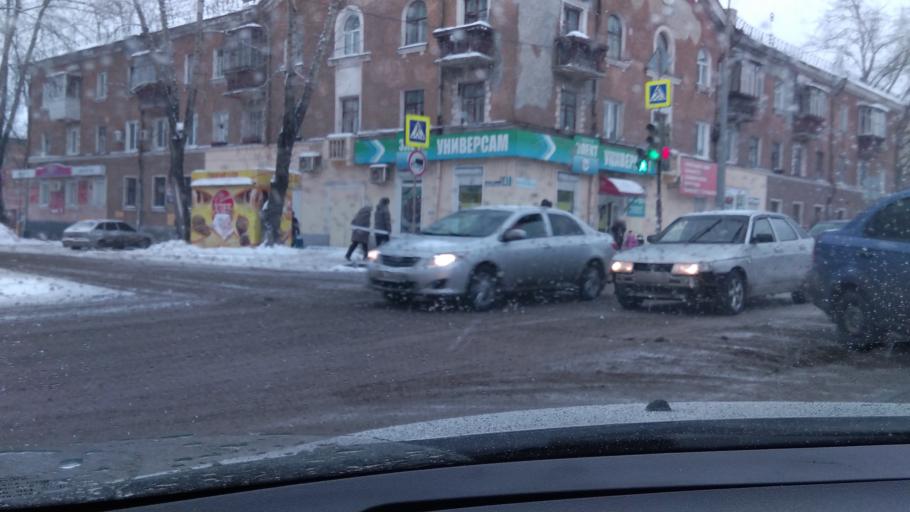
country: RU
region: Sverdlovsk
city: Yekaterinburg
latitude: 56.8978
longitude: 60.5782
